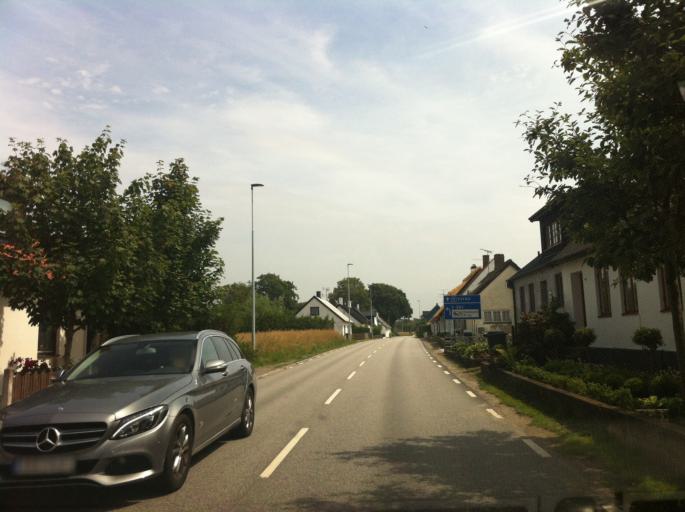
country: SE
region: Skane
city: Smygehamn
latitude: 55.3450
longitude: 13.2869
